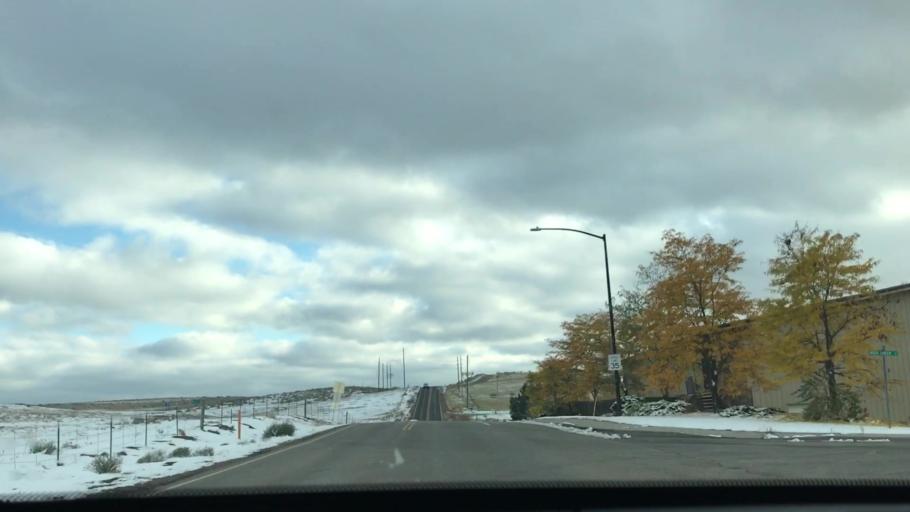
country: US
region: Colorado
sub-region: Boulder County
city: Lafayette
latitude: 39.9733
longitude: -105.0719
